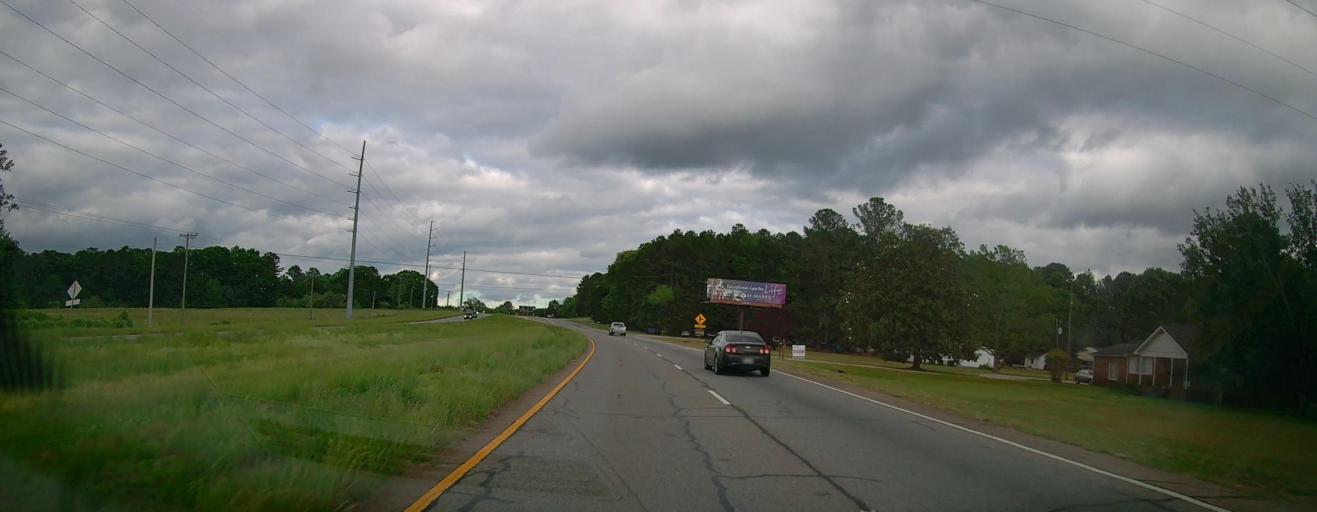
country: US
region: Georgia
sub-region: Oconee County
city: Bogart
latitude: 33.9180
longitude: -83.5240
